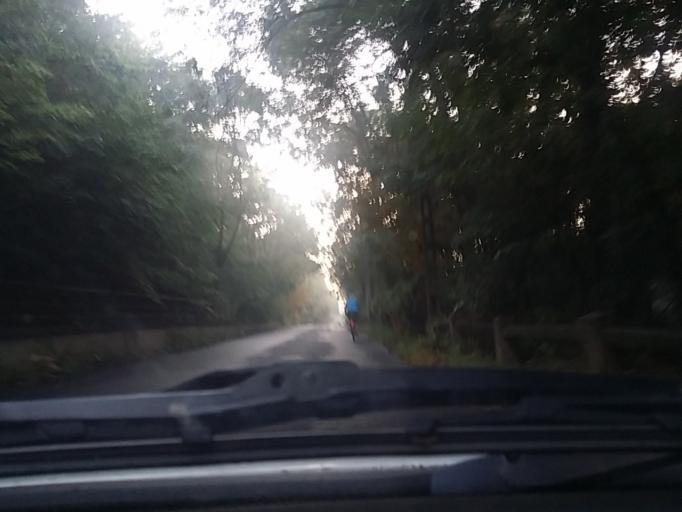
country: HU
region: Budapest
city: Budapest II. keruelet
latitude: 47.5400
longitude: 19.0078
